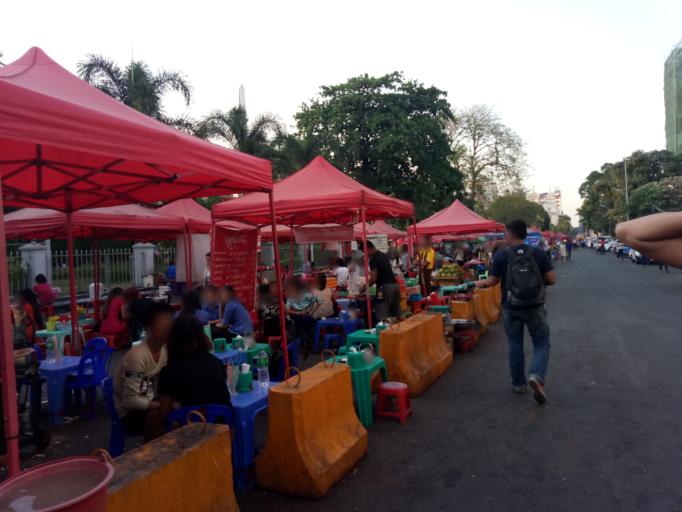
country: MM
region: Yangon
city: Yangon
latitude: 16.7721
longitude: 96.1602
